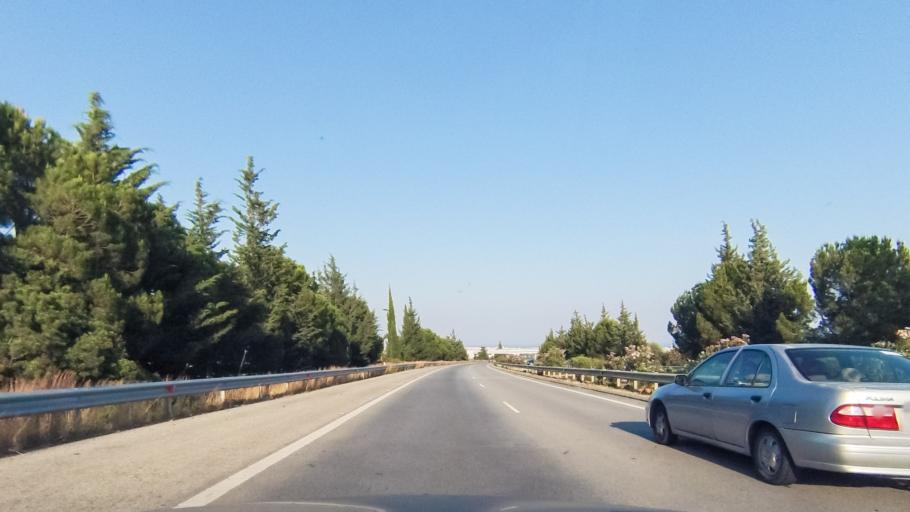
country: CY
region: Limassol
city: Ypsonas
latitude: 34.6968
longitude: 32.9615
